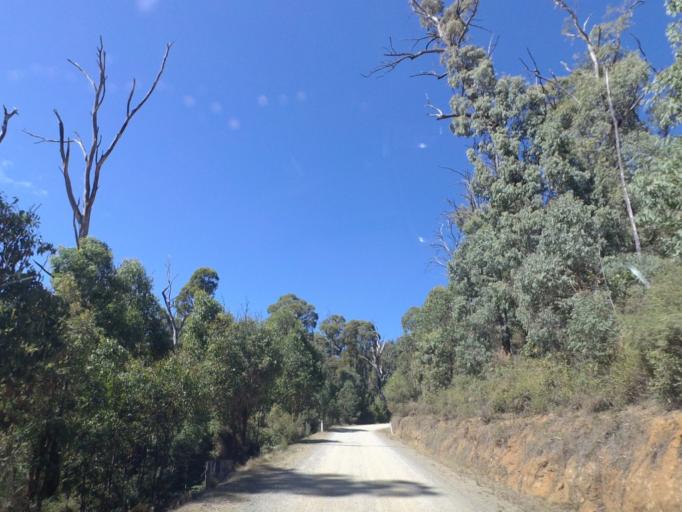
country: AU
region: Victoria
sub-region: Yarra Ranges
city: Millgrove
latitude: -37.5299
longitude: 145.7500
